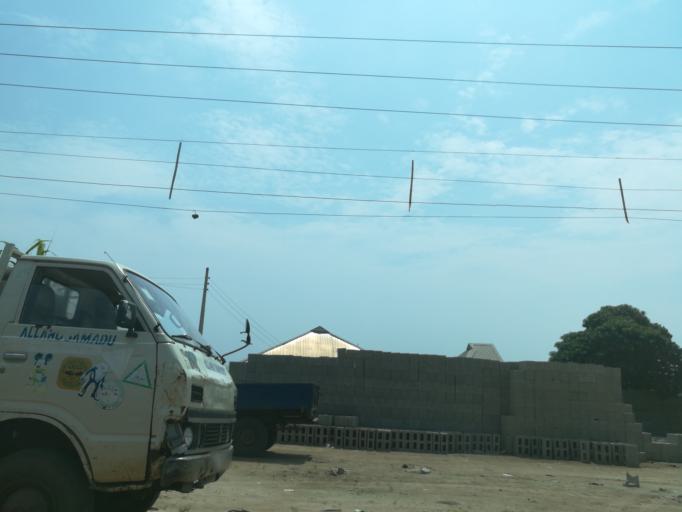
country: NG
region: Lagos
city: Ikorodu
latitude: 6.5793
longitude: 3.6274
